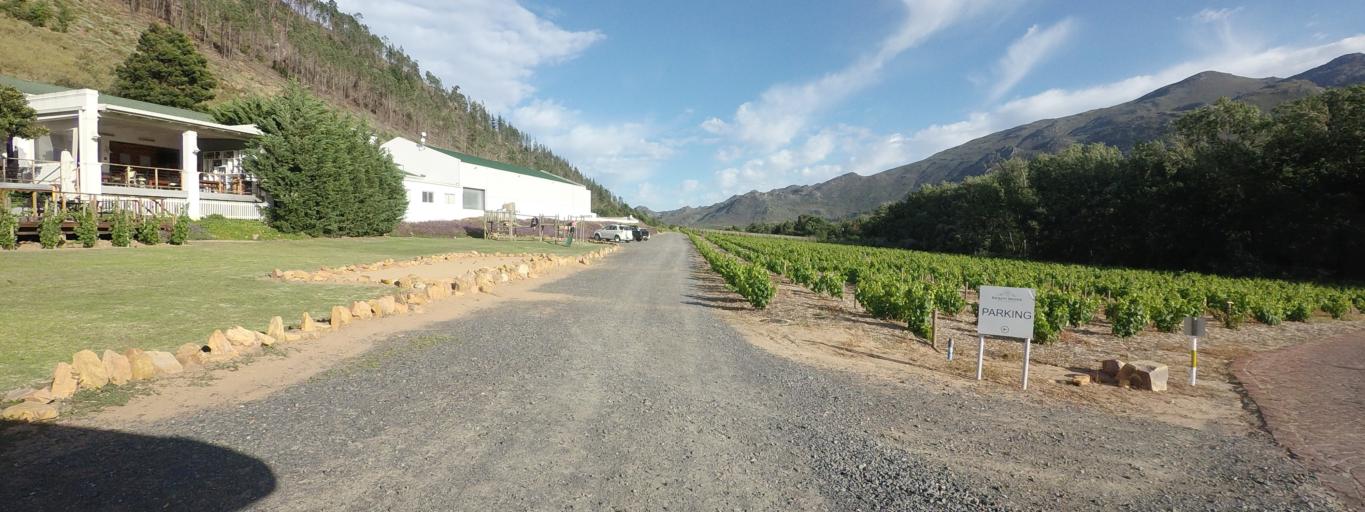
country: ZA
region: Western Cape
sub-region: Cape Winelands District Municipality
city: Paarl
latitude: -33.8989
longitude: 19.0915
